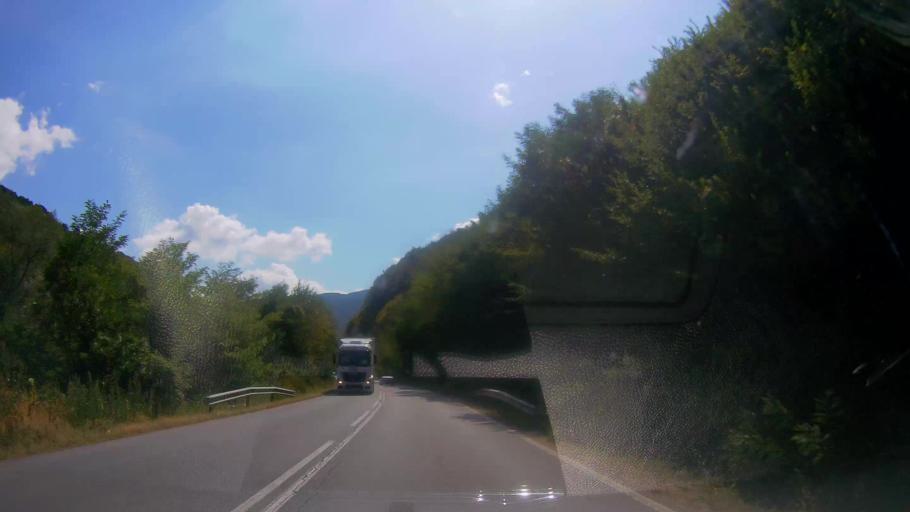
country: BG
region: Stara Zagora
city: Gurkovo
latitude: 42.7258
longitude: 25.7125
